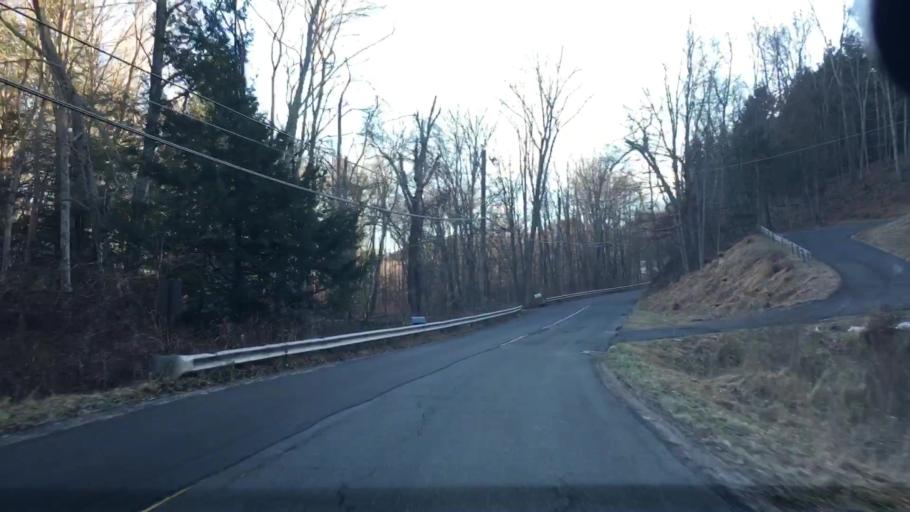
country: US
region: Connecticut
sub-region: Fairfield County
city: Newtown
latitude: 41.4550
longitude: -73.3247
